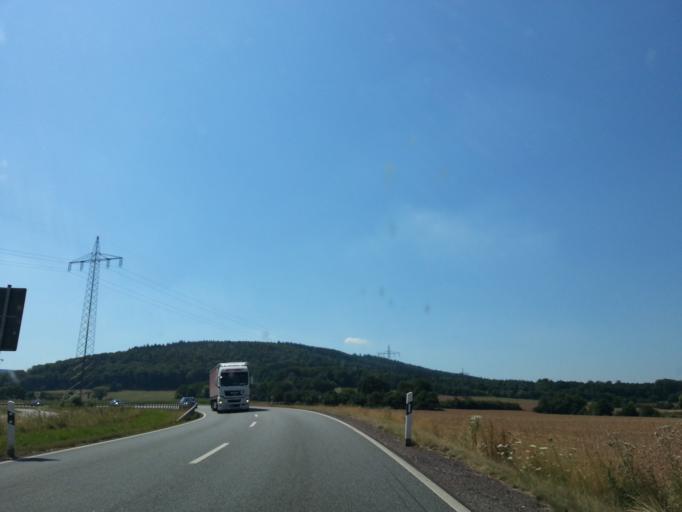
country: DE
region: Rheinland-Pfalz
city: Altrich
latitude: 49.9485
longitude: 6.9254
